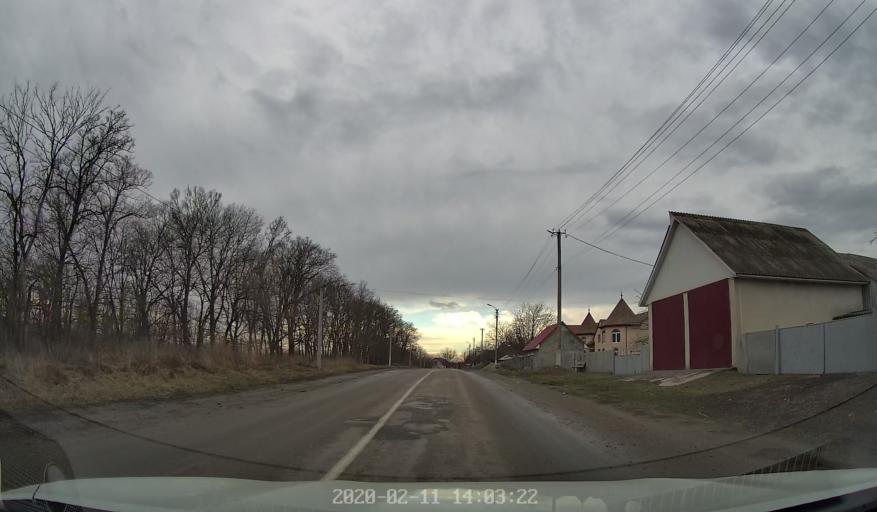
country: RO
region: Botosani
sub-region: Comuna Paltinis
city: Paltinis
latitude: 48.2585
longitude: 26.5994
